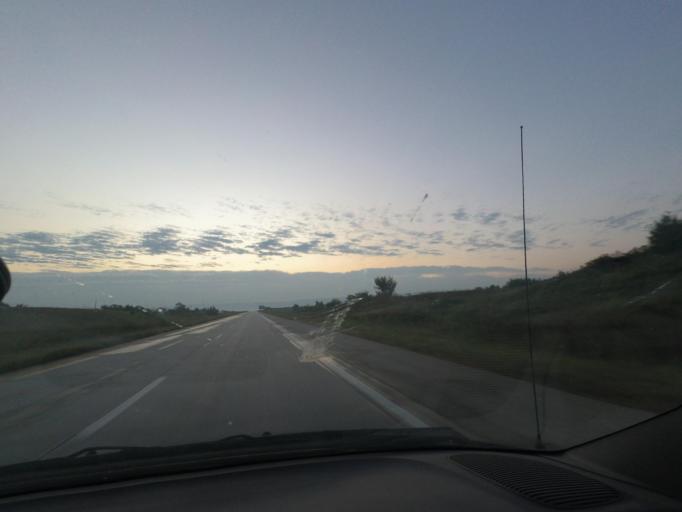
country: US
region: Missouri
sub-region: Linn County
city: Marceline
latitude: 39.7649
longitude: -92.7790
